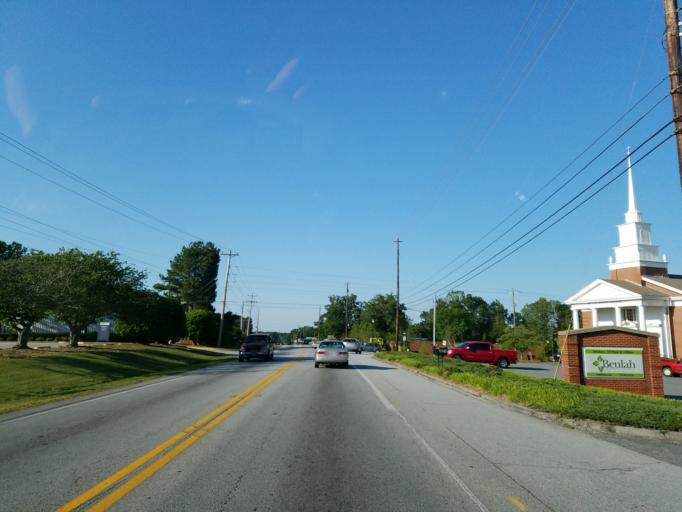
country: US
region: Georgia
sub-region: Douglas County
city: Lithia Springs
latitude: 33.7794
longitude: -84.7043
